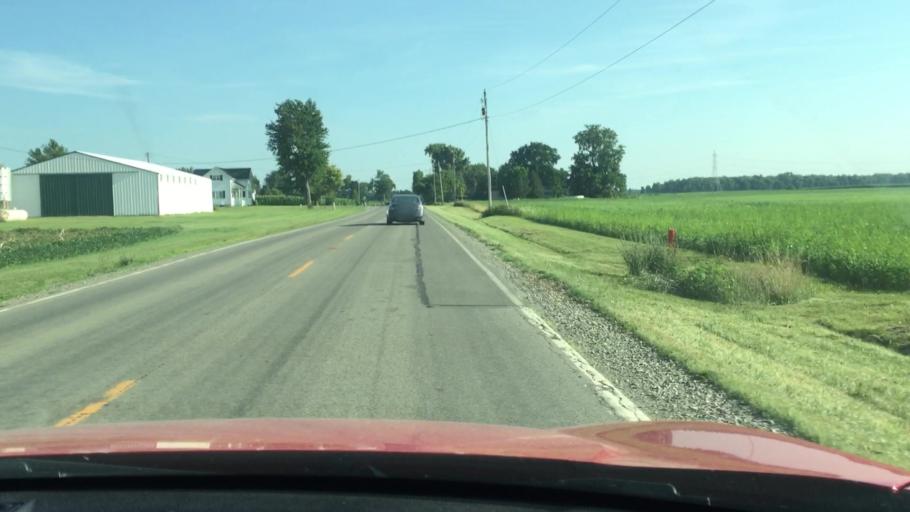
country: US
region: Ohio
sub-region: Hardin County
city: Ada
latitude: 40.6882
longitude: -83.8571
